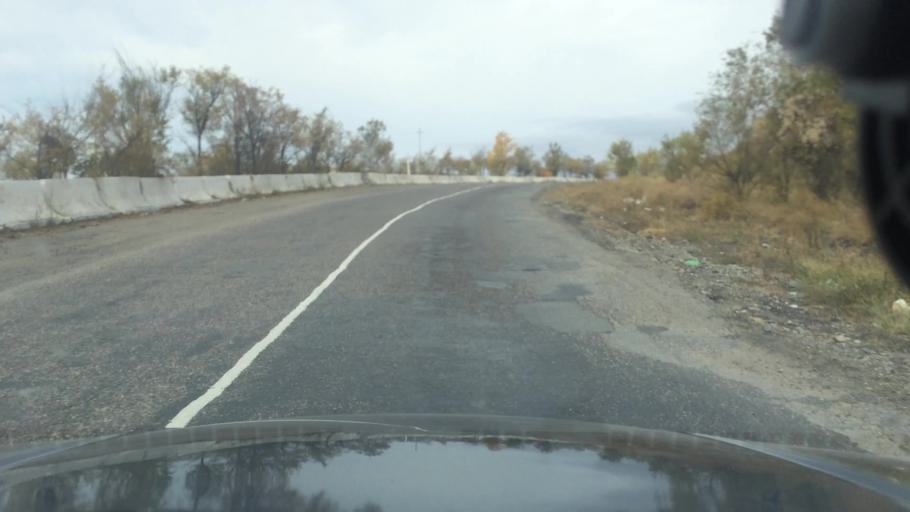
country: KG
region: Ysyk-Koel
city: Karakol
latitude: 42.5970
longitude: 78.3774
